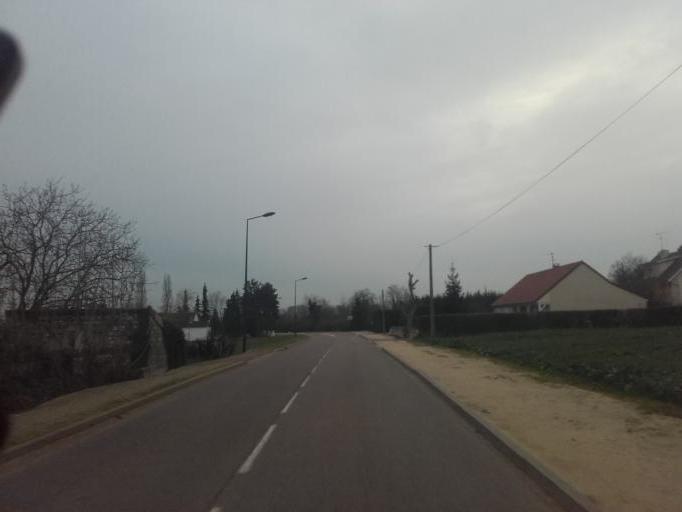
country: FR
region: Bourgogne
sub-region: Departement de Saone-et-Loire
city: Fontaines
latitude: 46.8465
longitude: 4.7530
